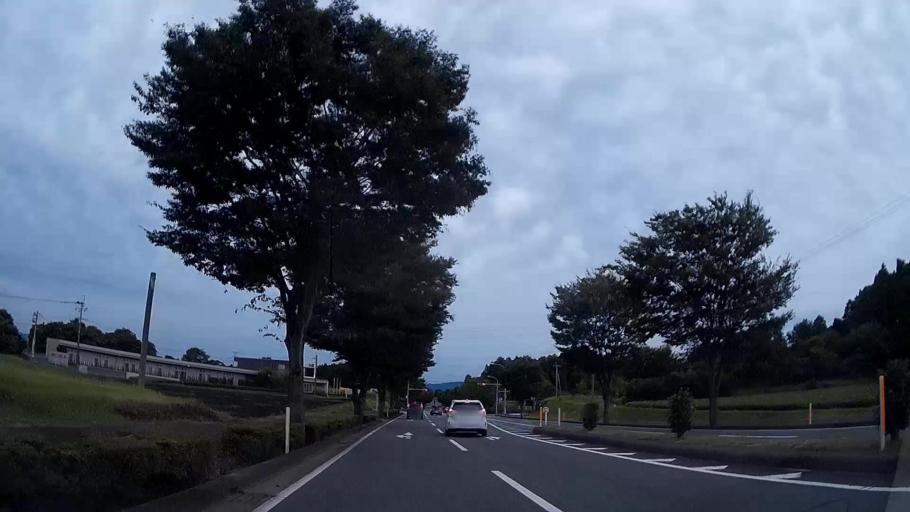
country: JP
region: Kumamoto
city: Ozu
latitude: 32.9153
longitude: 130.8405
